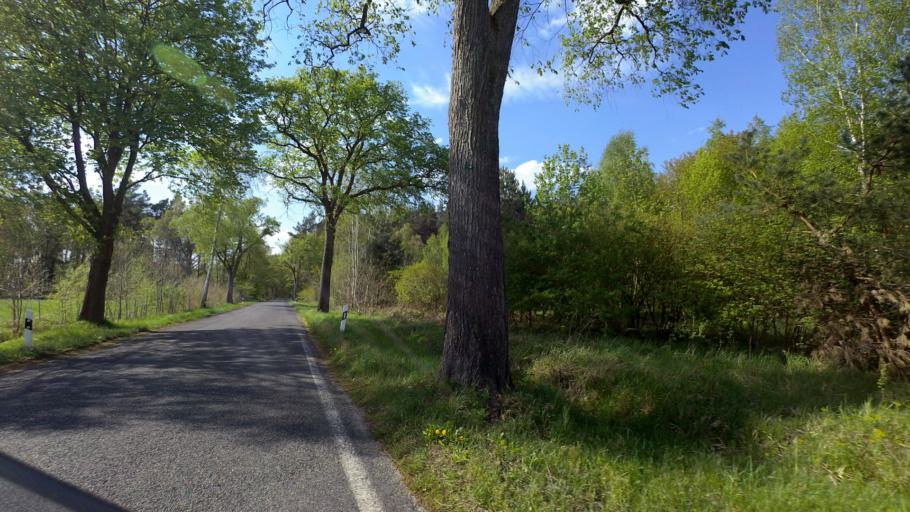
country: DE
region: Brandenburg
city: Templin
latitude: 53.0060
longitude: 13.4639
